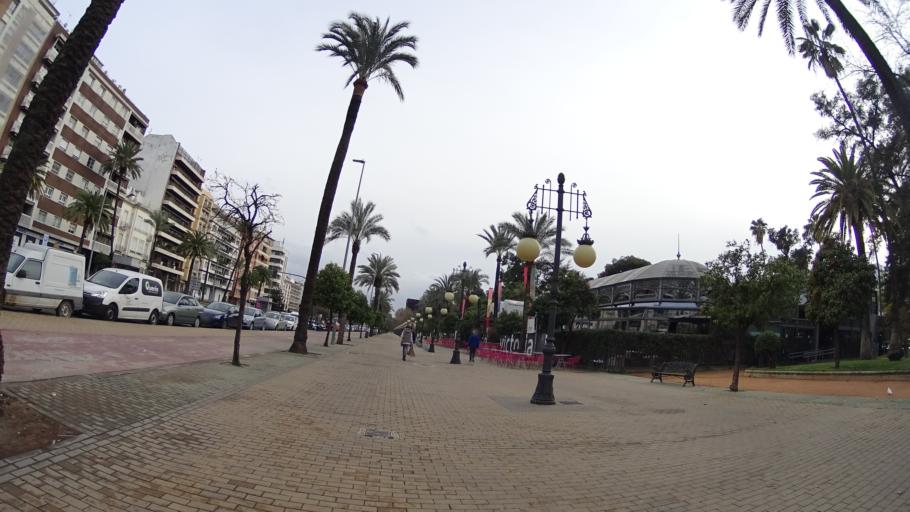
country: ES
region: Andalusia
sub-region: Province of Cordoba
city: Cordoba
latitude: 37.8839
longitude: -4.7850
